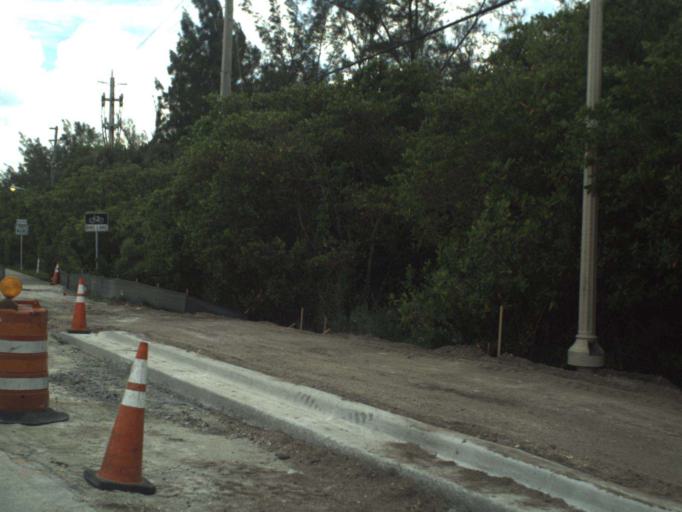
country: US
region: Florida
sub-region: Martin County
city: Jensen Beach
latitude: 27.2554
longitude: -80.1978
